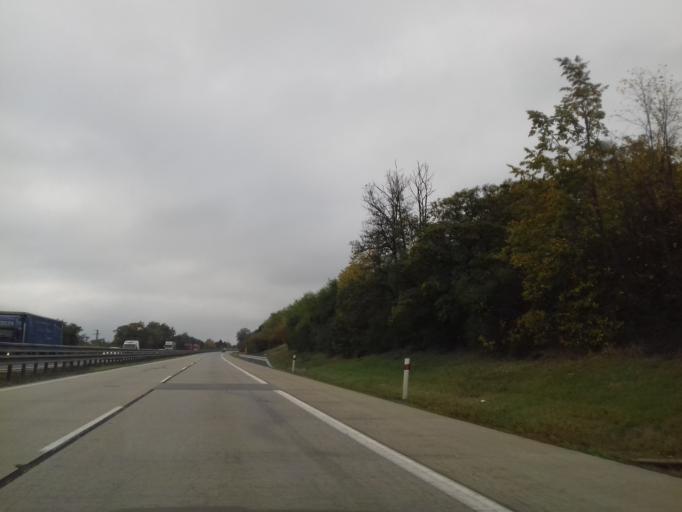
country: CZ
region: South Moravian
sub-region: Okres Breclav
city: Hustopece
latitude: 48.9321
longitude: 16.7507
